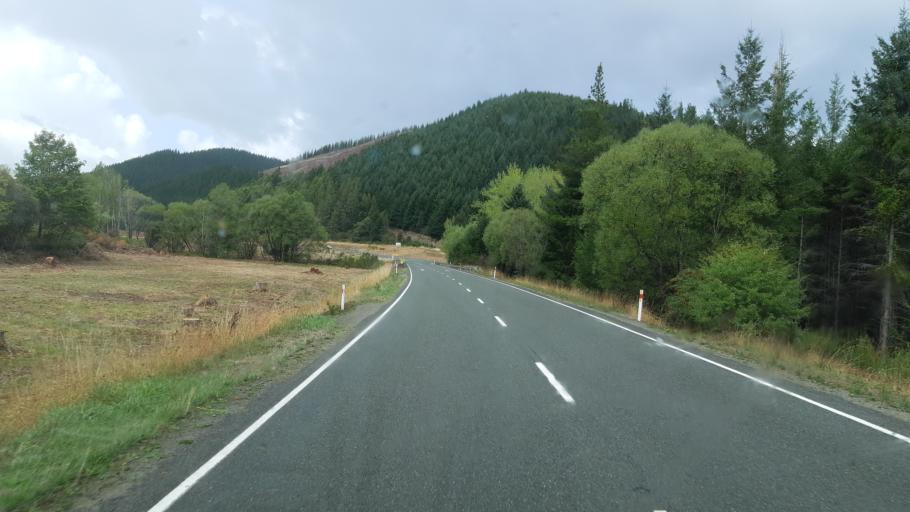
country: NZ
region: Tasman
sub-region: Tasman District
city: Wakefield
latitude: -41.4717
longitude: 172.8430
